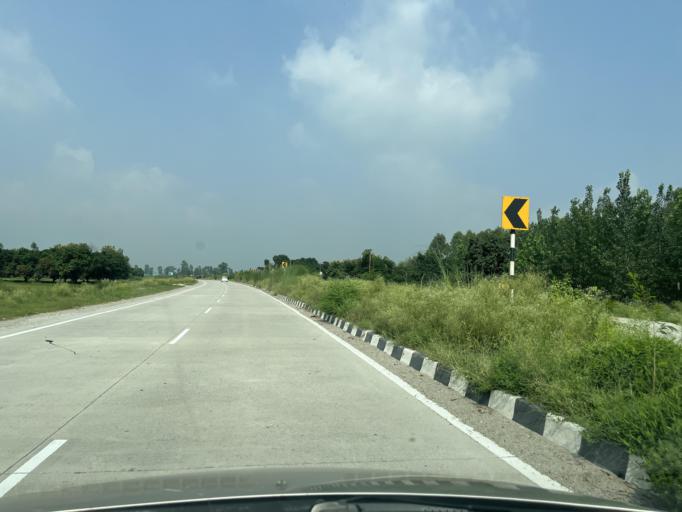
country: IN
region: Uttarakhand
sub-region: Udham Singh Nagar
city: Kashipur
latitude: 29.1663
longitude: 78.9854
